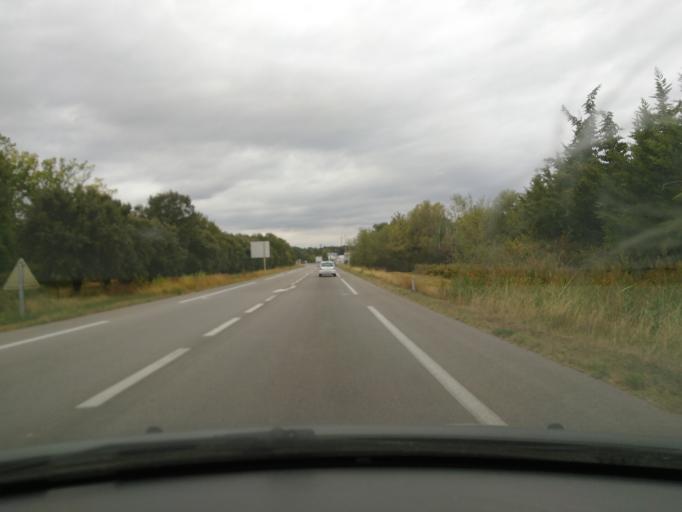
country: FR
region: Provence-Alpes-Cote d'Azur
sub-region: Departement du Vaucluse
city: Grillon
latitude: 44.3953
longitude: 4.9403
